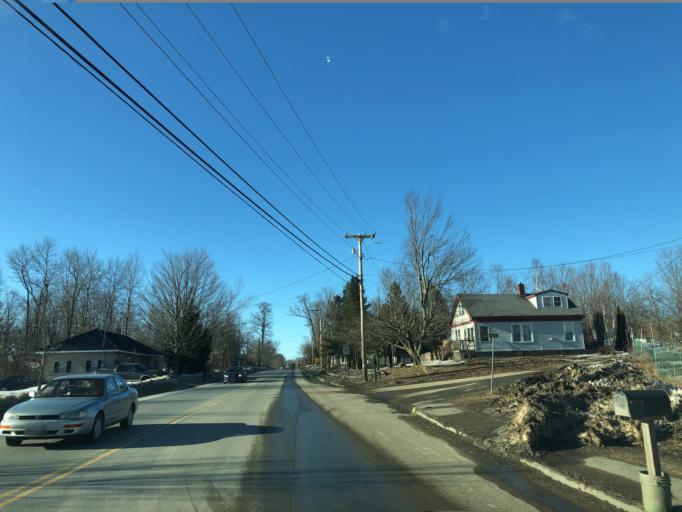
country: US
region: Maine
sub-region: Penobscot County
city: Kenduskeag
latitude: 44.9196
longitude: -68.9310
